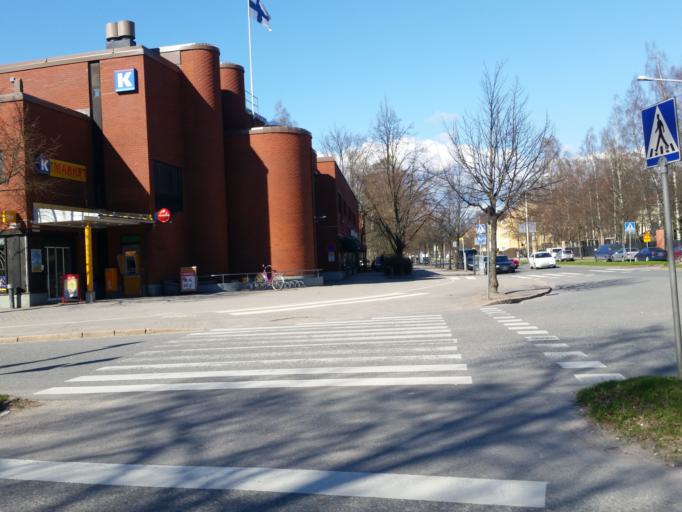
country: FI
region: Uusimaa
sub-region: Helsinki
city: Helsinki
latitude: 60.2156
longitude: 24.9583
